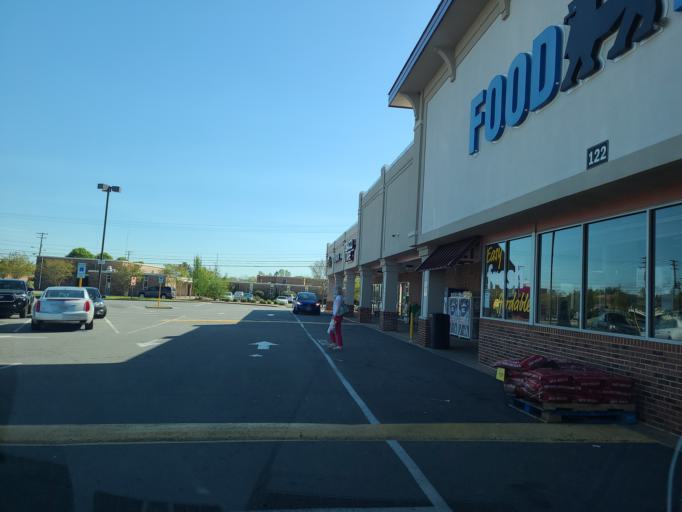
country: US
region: North Carolina
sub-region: Cleveland County
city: Shelby
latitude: 35.2829
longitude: -81.4930
